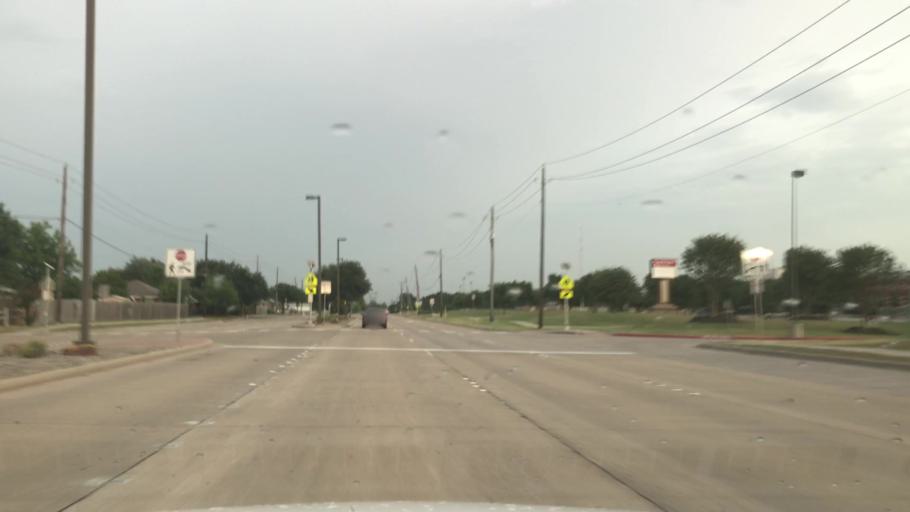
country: US
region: Texas
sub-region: Dallas County
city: Mesquite
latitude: 32.7333
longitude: -96.5573
